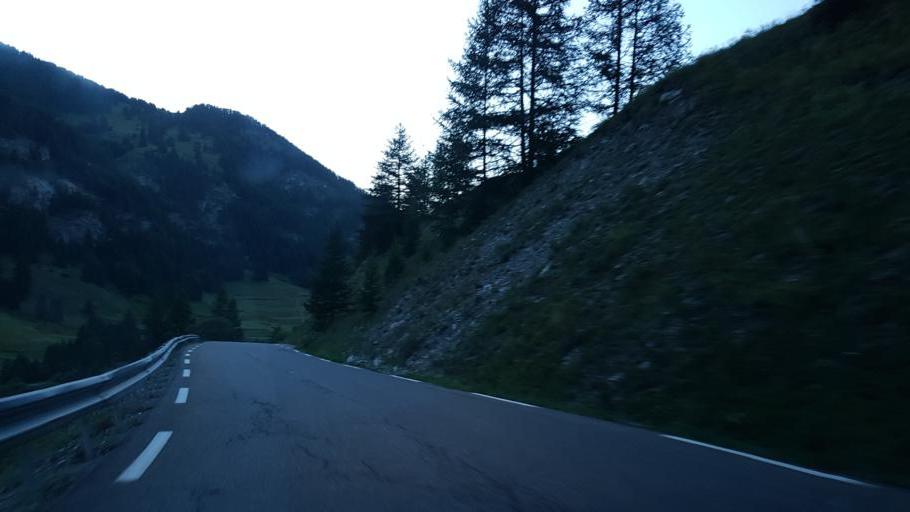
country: IT
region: Piedmont
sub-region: Provincia di Cuneo
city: Pontechianale
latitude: 44.7065
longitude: 6.8526
